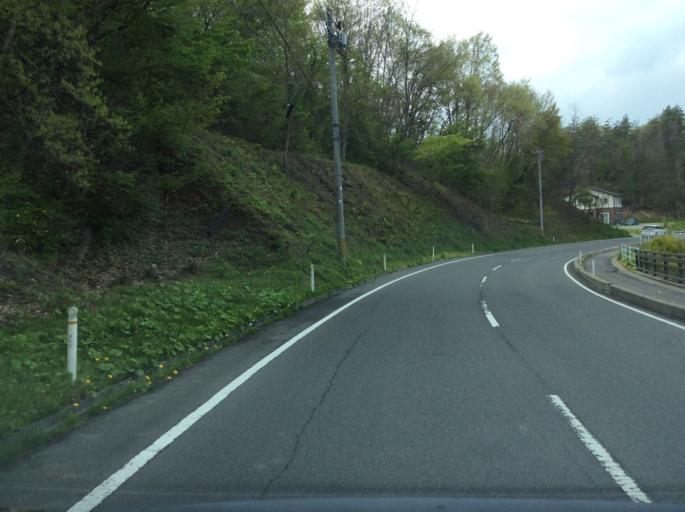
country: JP
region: Fukushima
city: Miharu
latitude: 37.3957
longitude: 140.4827
